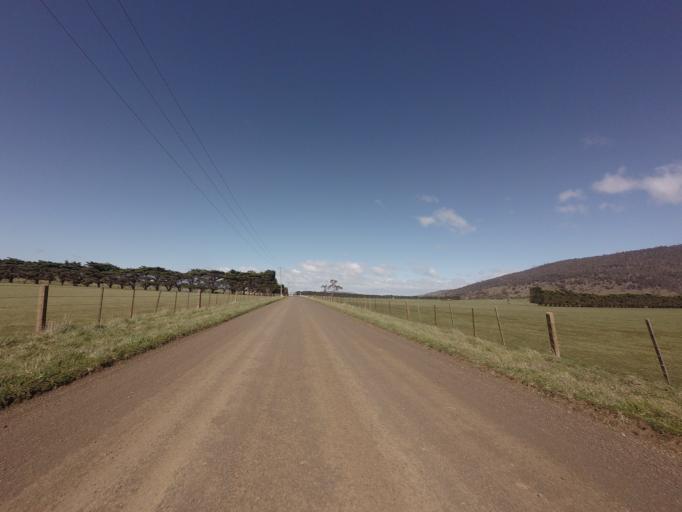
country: AU
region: Tasmania
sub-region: Northern Midlands
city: Evandale
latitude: -41.9606
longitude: 147.4383
